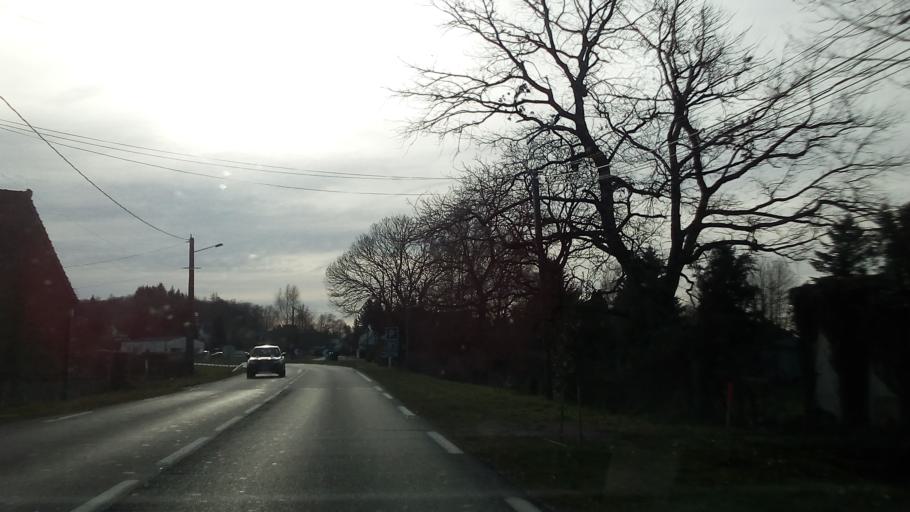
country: FR
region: Limousin
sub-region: Departement de la Correze
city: Naves
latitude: 45.3385
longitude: 1.7486
